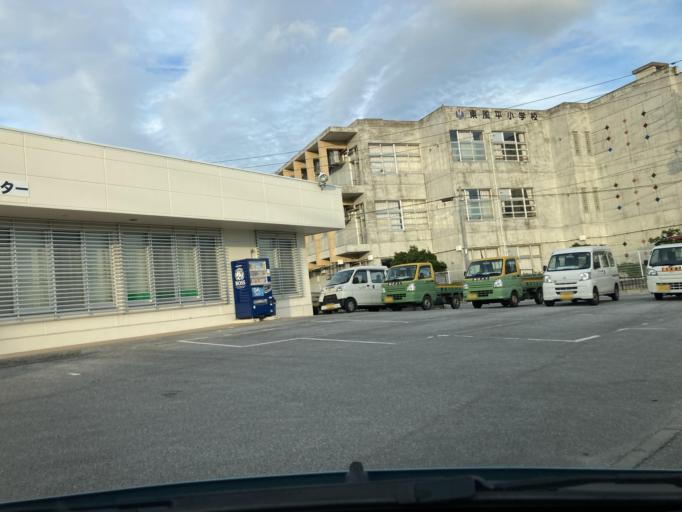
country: JP
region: Okinawa
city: Tomigusuku
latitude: 26.1537
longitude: 127.7214
